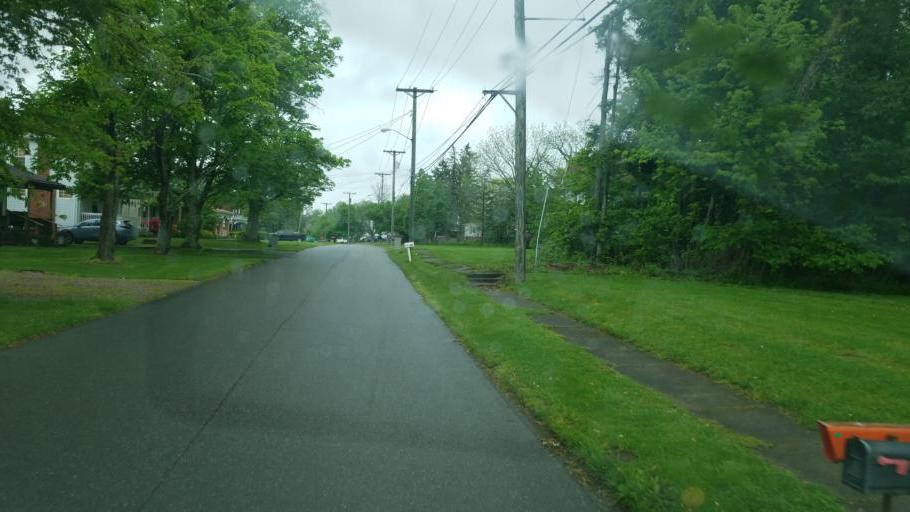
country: US
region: Ohio
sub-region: Jefferson County
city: Wintersville
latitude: 40.2711
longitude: -80.7723
